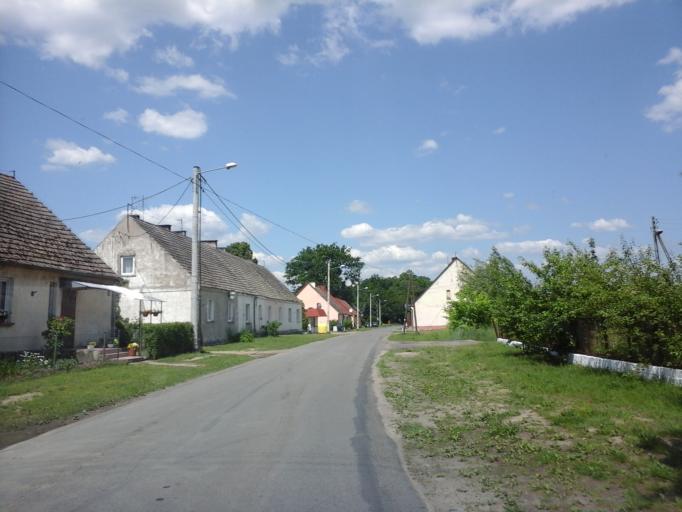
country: PL
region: West Pomeranian Voivodeship
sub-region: Powiat choszczenski
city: Bierzwnik
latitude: 53.1504
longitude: 15.6258
